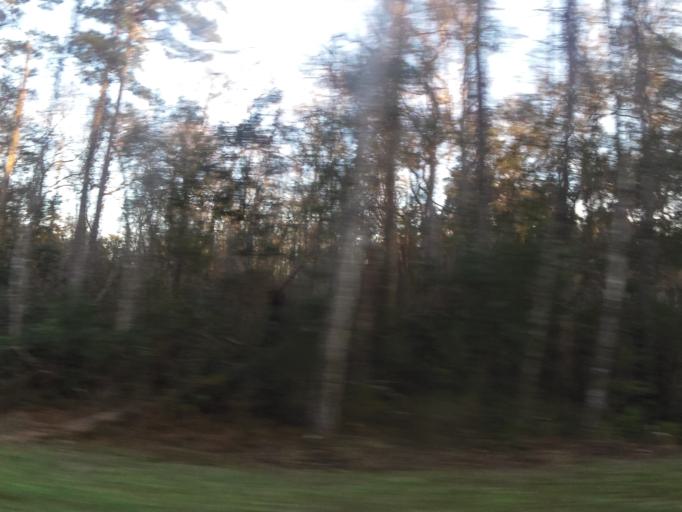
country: US
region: Florida
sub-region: Clay County
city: Green Cove Springs
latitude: 29.9346
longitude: -81.5695
